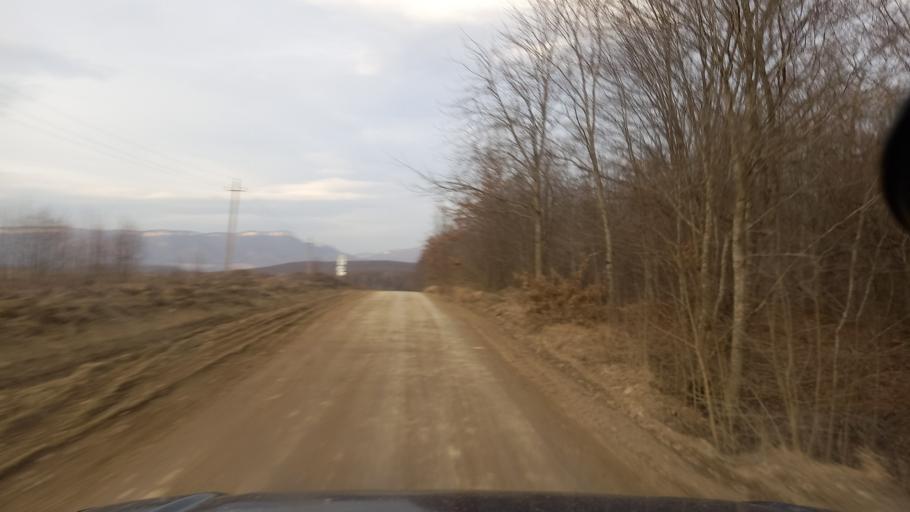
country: RU
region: Adygeya
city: Kamennomostskiy
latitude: 44.1562
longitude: 40.2422
